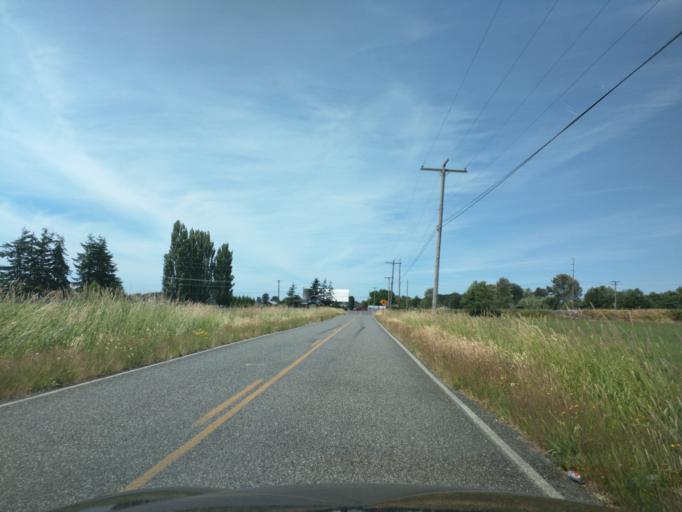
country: US
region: Washington
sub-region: Whatcom County
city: Lynden
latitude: 48.9351
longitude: -122.4388
